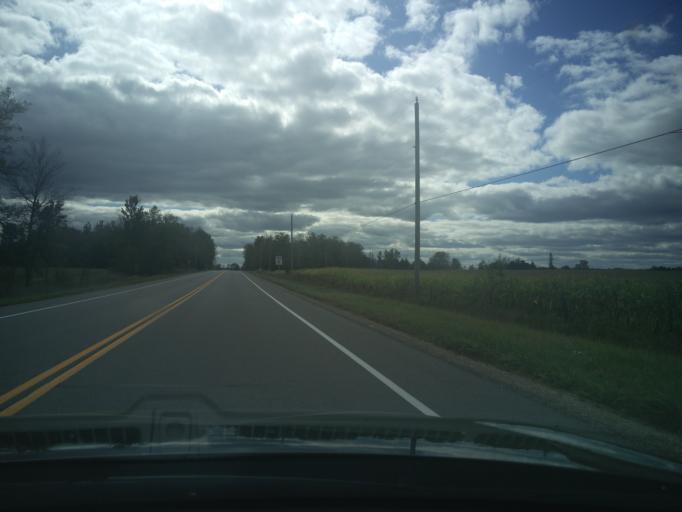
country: CA
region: Ontario
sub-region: Lanark County
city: Smiths Falls
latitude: 44.9966
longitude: -76.1018
